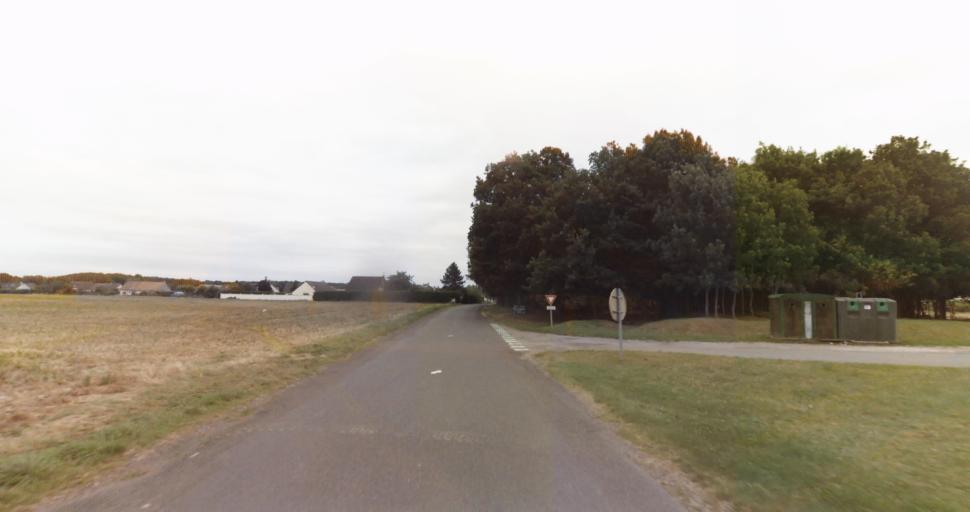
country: FR
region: Centre
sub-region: Departement d'Eure-et-Loir
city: Vert-en-Drouais
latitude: 48.7765
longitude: 1.2989
